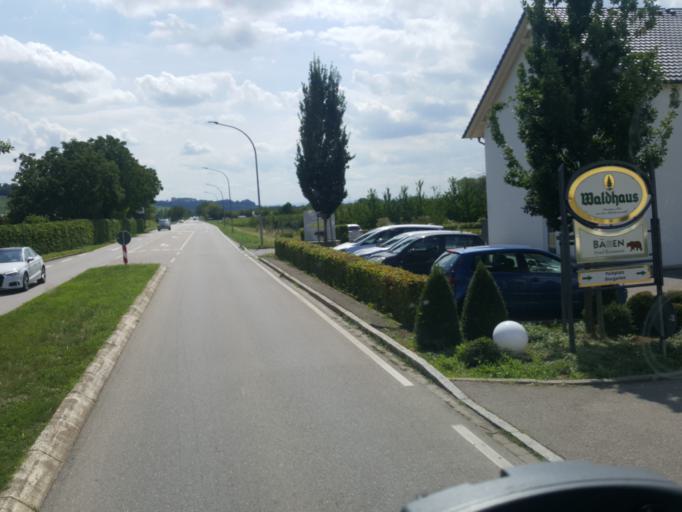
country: DE
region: Baden-Wuerttemberg
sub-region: Freiburg Region
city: Auggen
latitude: 47.7884
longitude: 7.5905
